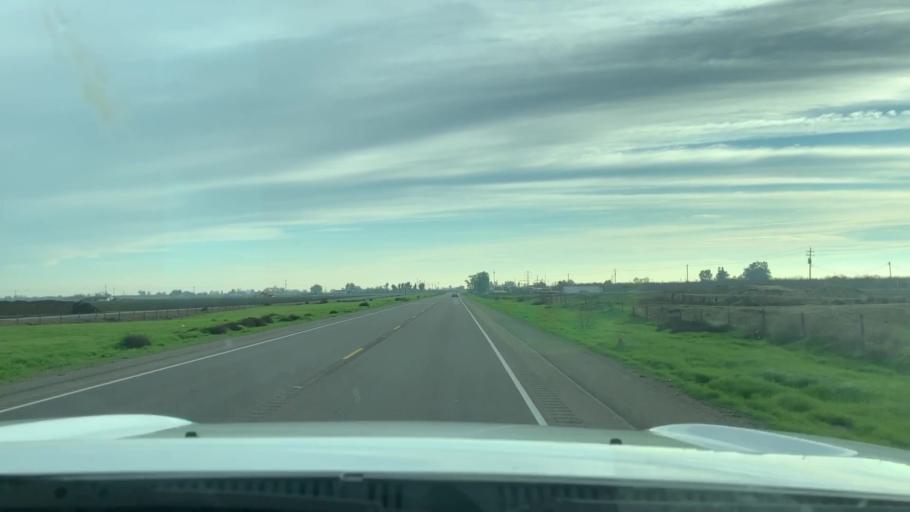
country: US
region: California
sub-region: Fresno County
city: Riverdale
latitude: 36.4529
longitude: -119.7970
